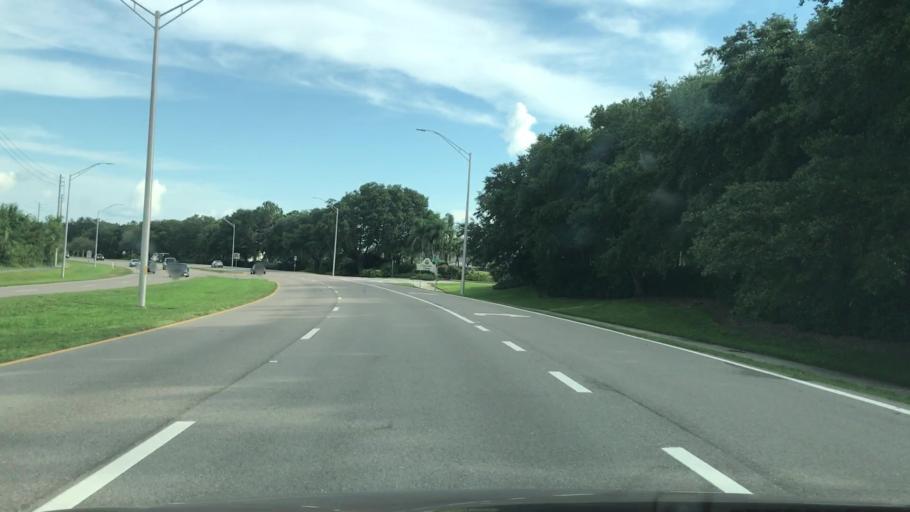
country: US
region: Florida
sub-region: Sarasota County
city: Venice Gardens
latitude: 27.0912
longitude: -82.3891
